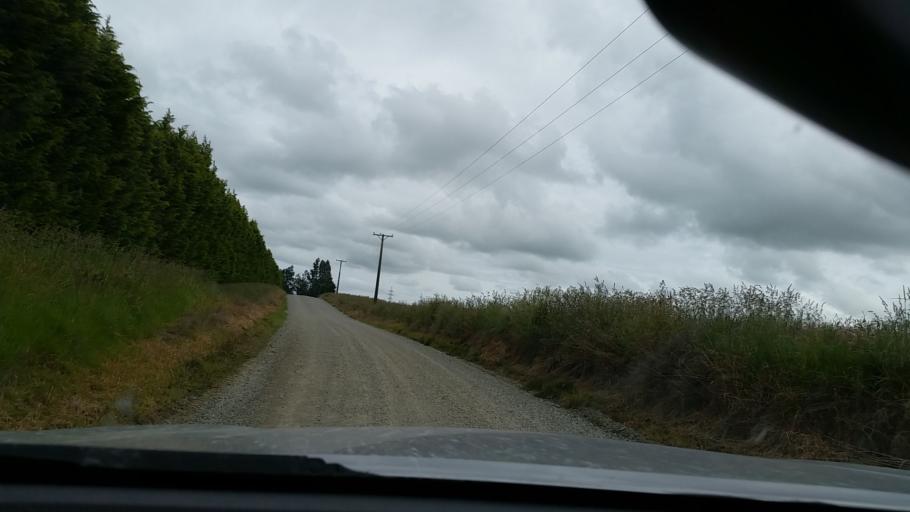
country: NZ
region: Southland
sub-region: Southland District
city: Winton
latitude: -46.1855
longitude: 168.1908
